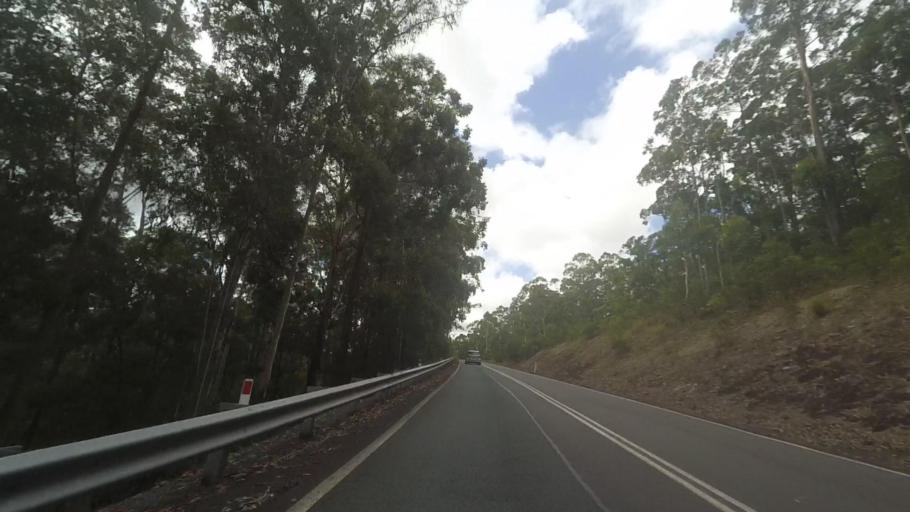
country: AU
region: New South Wales
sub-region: Great Lakes
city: Bulahdelah
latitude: -32.3940
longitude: 152.2464
